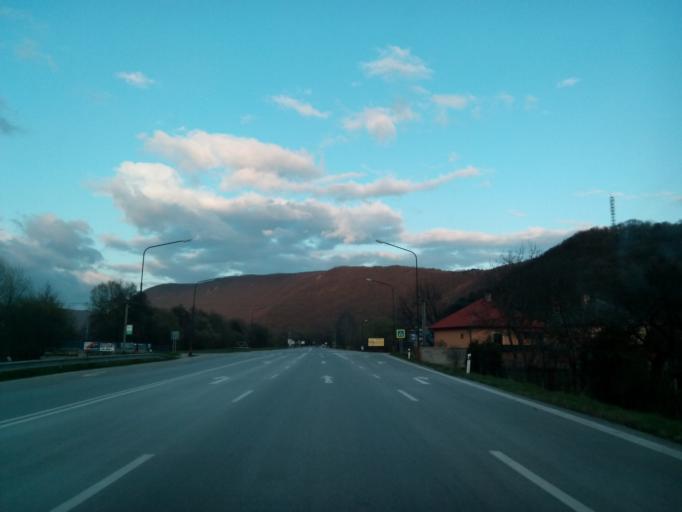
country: SK
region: Kosicky
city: Roznava
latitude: 48.5490
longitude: 20.4037
